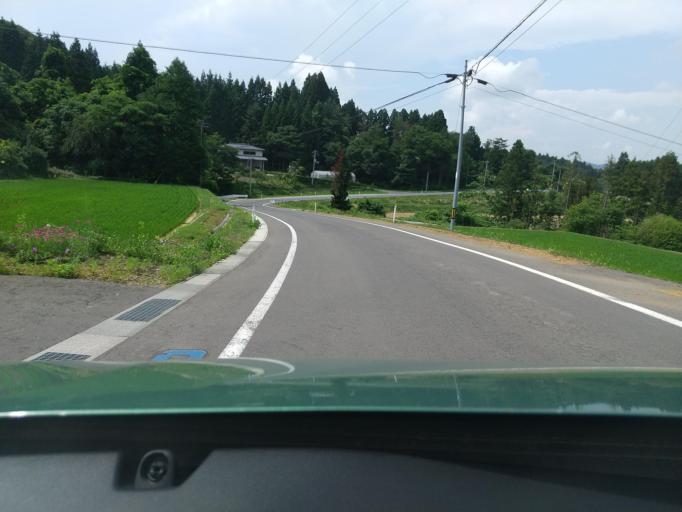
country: JP
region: Iwate
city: Ichinoseki
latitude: 39.0015
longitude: 141.2182
